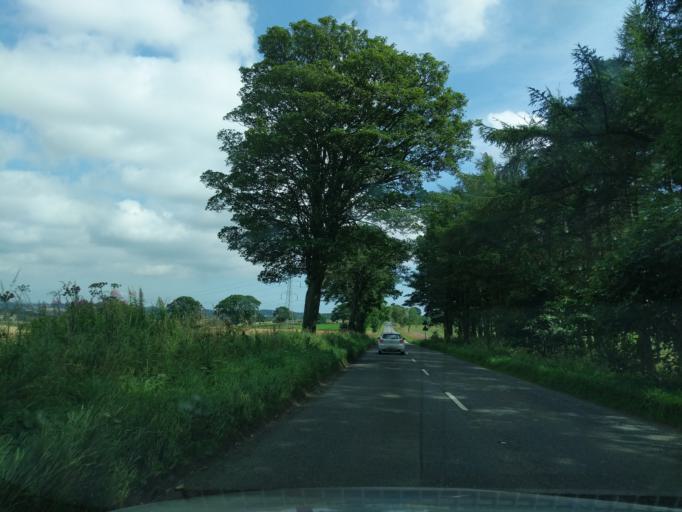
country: GB
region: Scotland
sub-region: Angus
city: Muirhead
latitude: 56.5033
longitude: -3.1179
